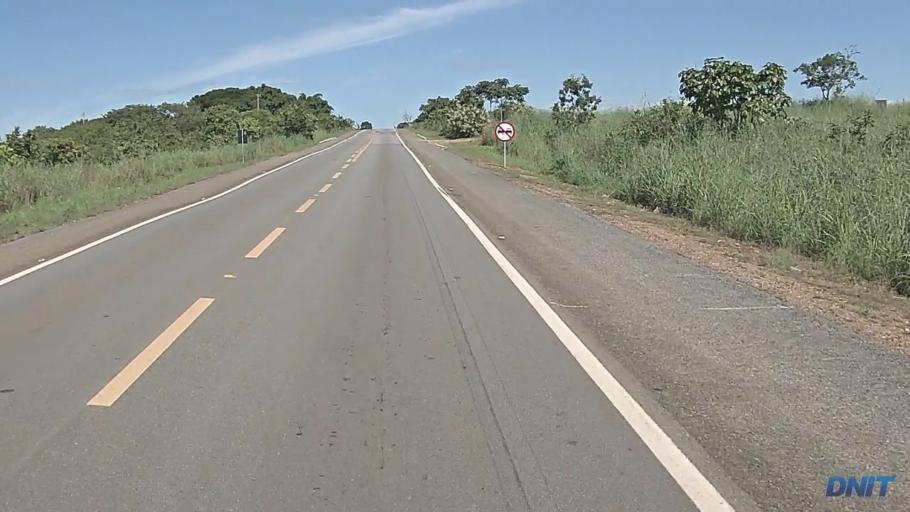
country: BR
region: Goias
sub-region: Padre Bernardo
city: Padre Bernardo
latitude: -15.2154
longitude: -48.5973
